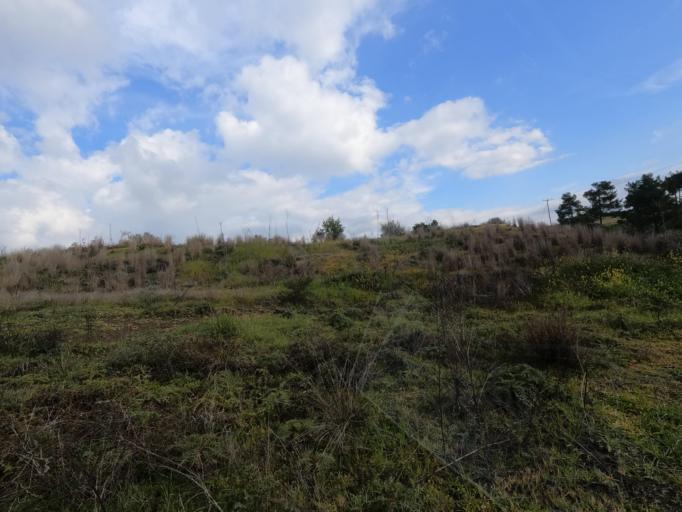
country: CY
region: Lefkosia
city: Kakopetria
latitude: 35.0713
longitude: 32.9450
